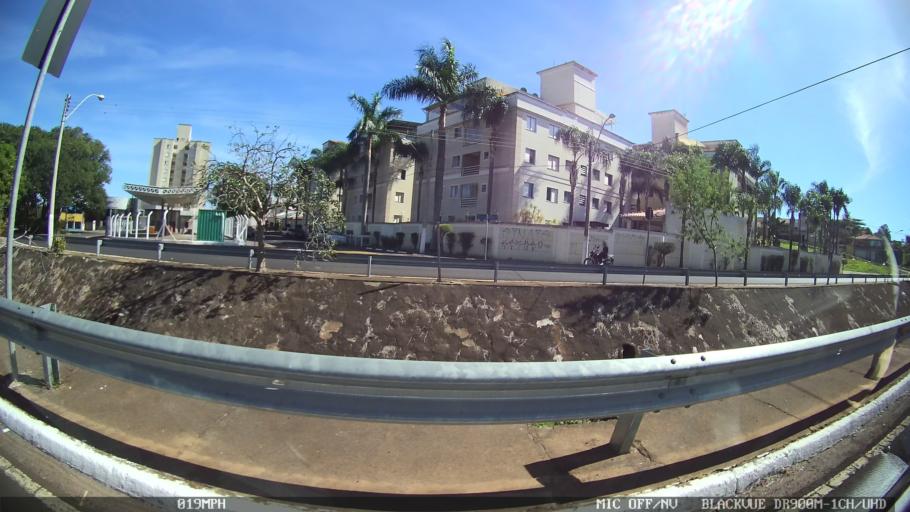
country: BR
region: Sao Paulo
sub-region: Franca
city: Franca
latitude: -20.5345
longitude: -47.3772
